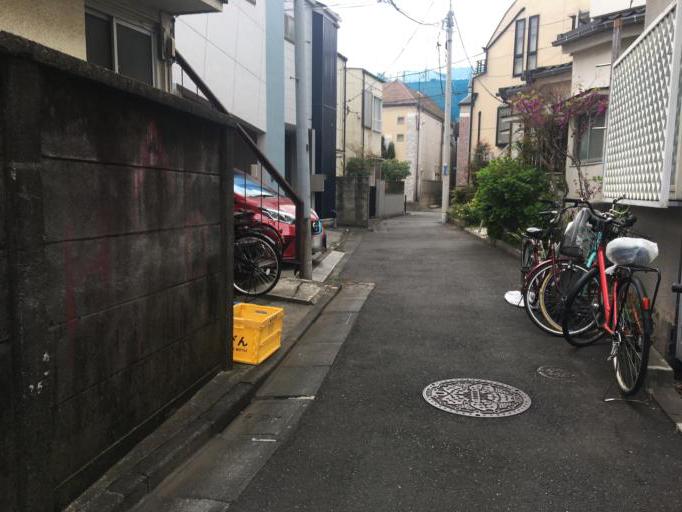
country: JP
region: Tokyo
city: Tokyo
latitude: 35.7014
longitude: 139.6611
